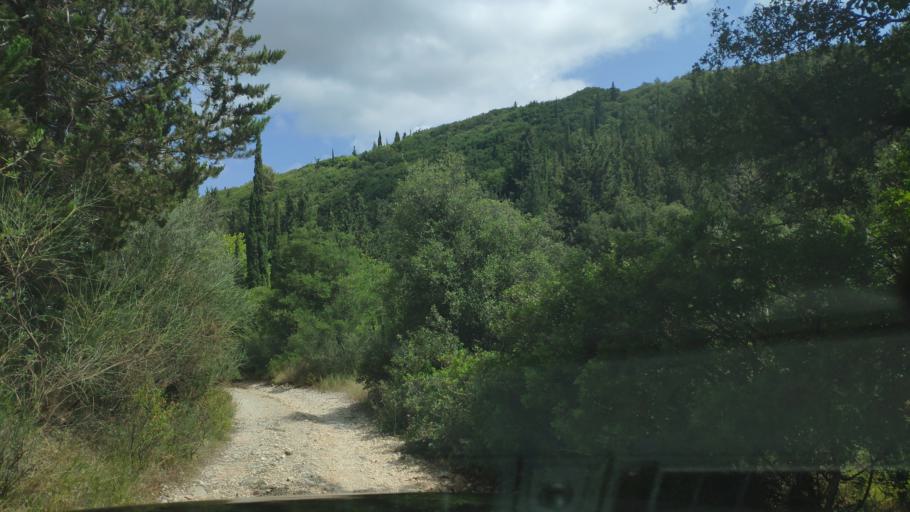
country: GR
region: Ionian Islands
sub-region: Lefkada
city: Lefkada
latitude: 38.7970
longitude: 20.6738
